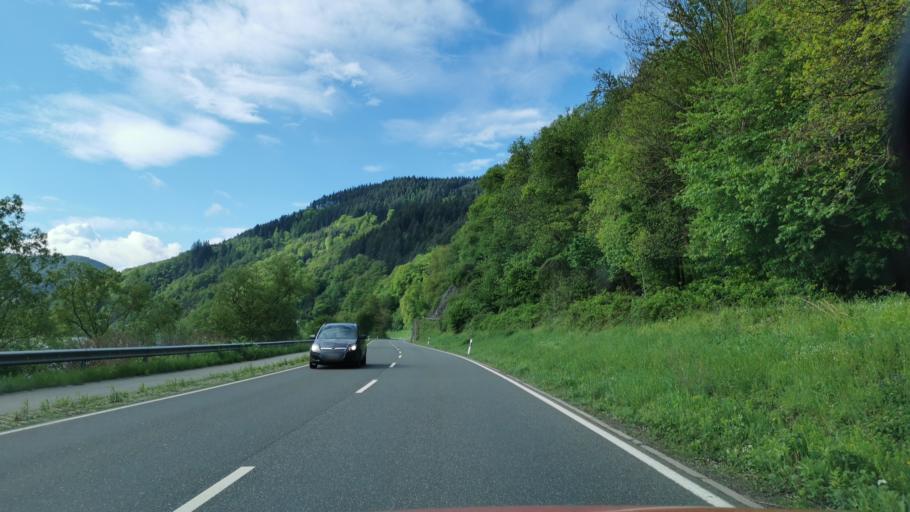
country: DE
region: Rheinland-Pfalz
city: Traben-Trarbach
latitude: 49.9620
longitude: 7.0995
